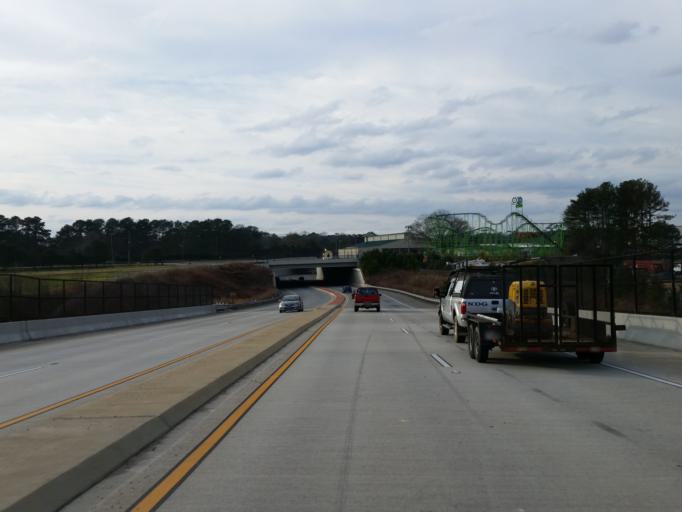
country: US
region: Georgia
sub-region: Cobb County
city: Fair Oaks
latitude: 33.8959
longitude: -84.5873
